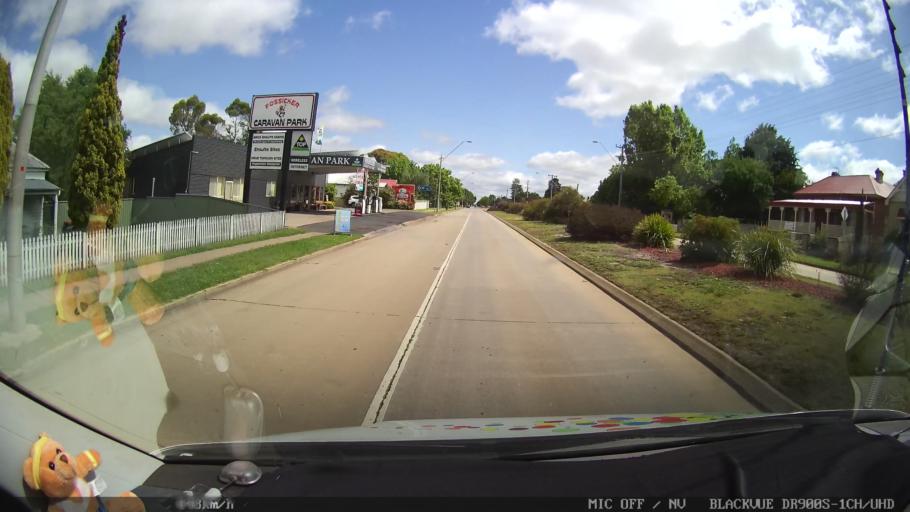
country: AU
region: New South Wales
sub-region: Glen Innes Severn
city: Glen Innes
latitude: -29.7451
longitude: 151.7368
